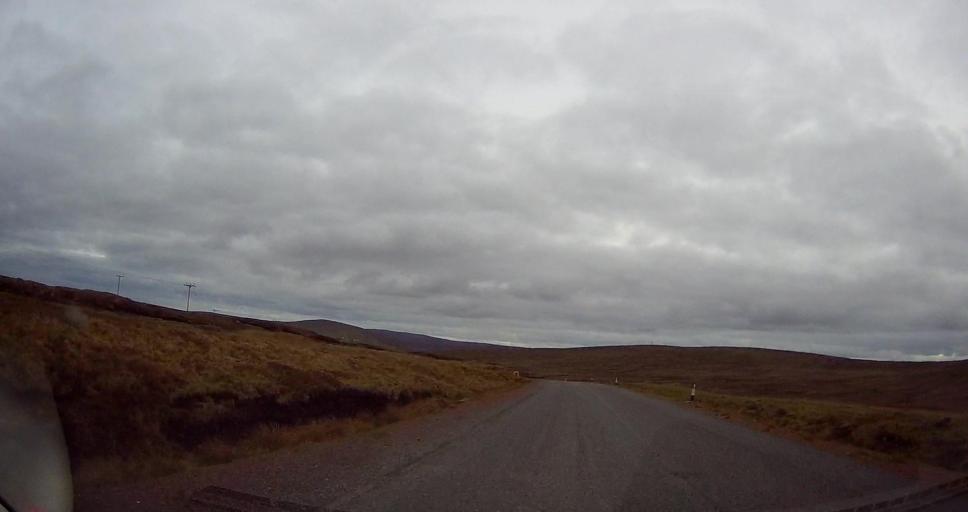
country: GB
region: Scotland
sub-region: Shetland Islands
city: Shetland
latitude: 60.6259
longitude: -1.0720
